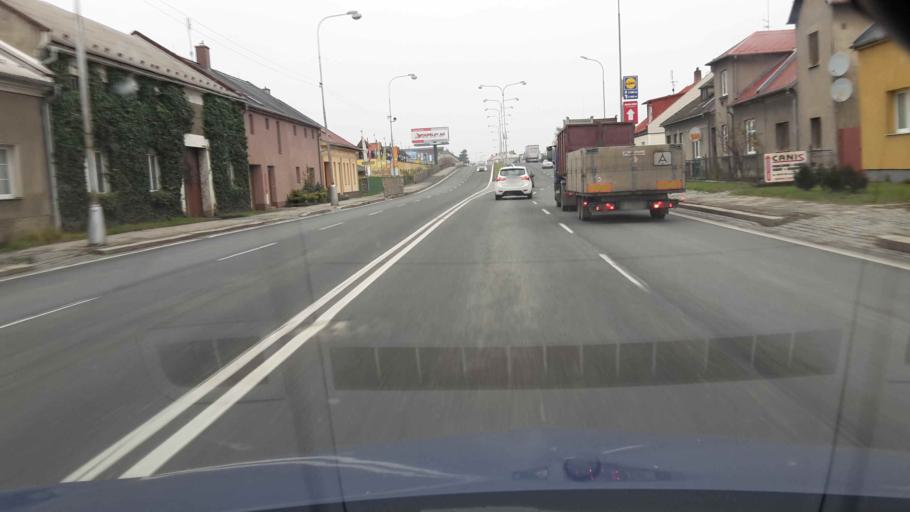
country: CZ
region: Olomoucky
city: Grygov
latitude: 49.5784
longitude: 17.2951
